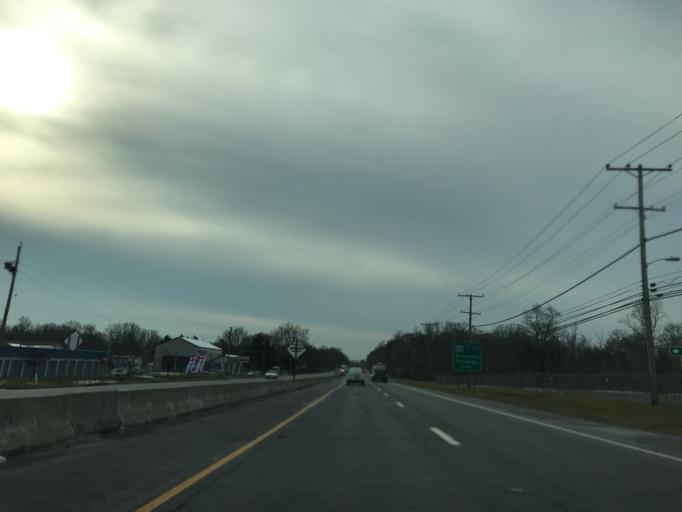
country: US
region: Maryland
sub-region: Harford County
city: Perryman
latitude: 39.4813
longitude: -76.2142
